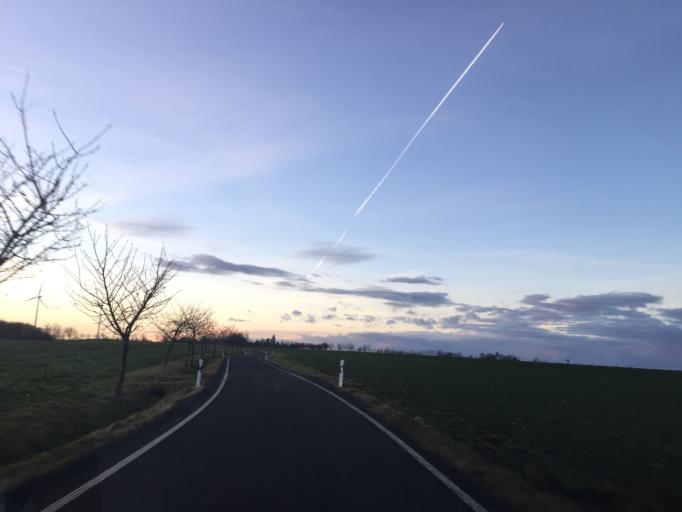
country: DE
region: Thuringia
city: Schmolln
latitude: 50.9002
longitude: 12.3404
